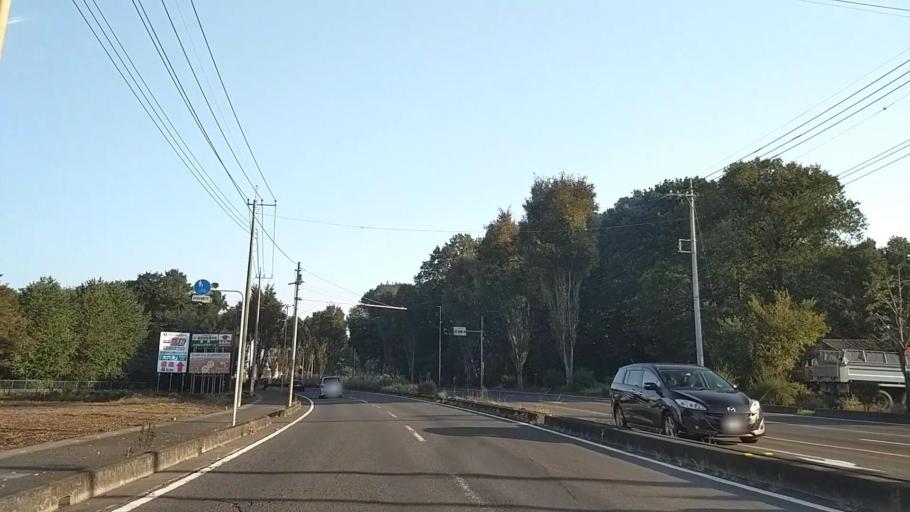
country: JP
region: Saitama
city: Sayama
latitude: 35.8114
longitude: 139.3990
